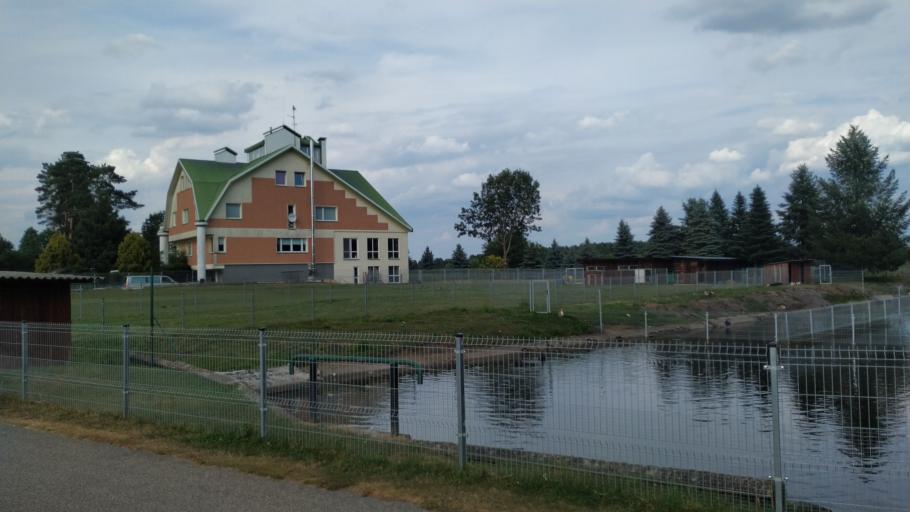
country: LT
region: Alytaus apskritis
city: Druskininkai
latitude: 54.0225
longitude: 24.0782
